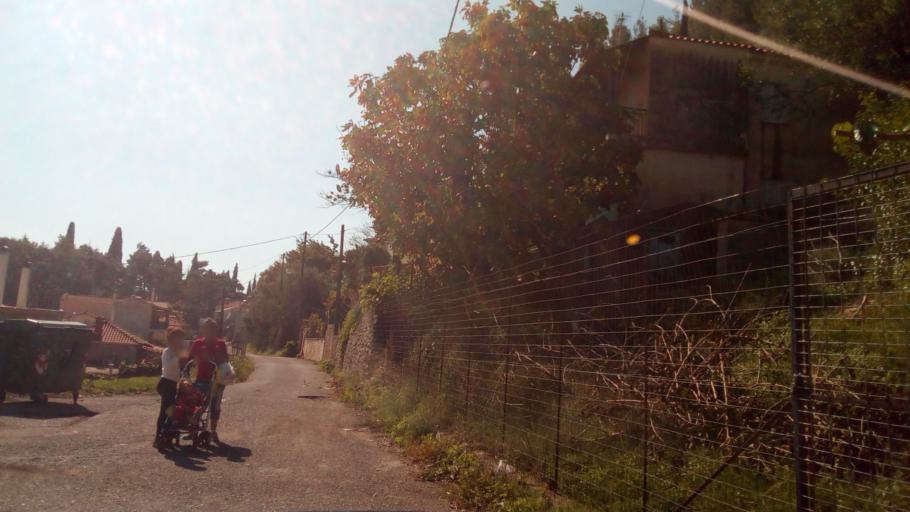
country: GR
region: West Greece
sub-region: Nomos Aitolias kai Akarnanias
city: Nafpaktos
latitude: 38.3977
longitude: 21.8409
